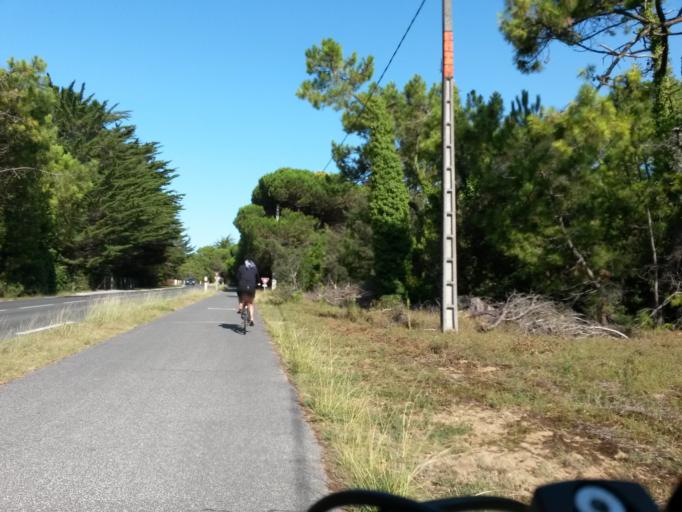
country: FR
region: Poitou-Charentes
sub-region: Departement de la Charente-Maritime
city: Saint-Martin-de-Re
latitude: 46.1730
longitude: -1.3654
